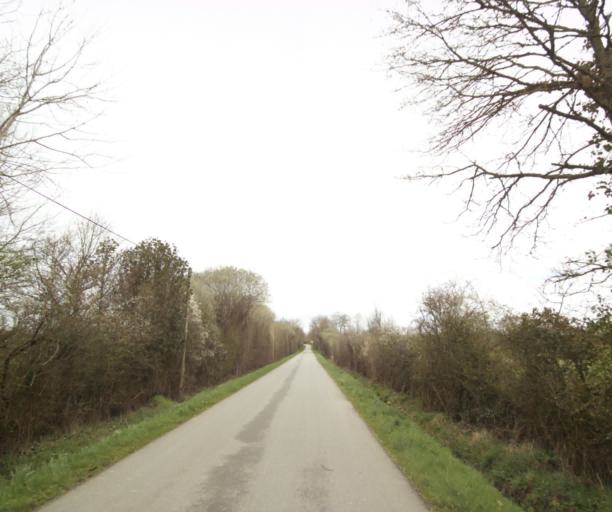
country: FR
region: Pays de la Loire
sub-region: Departement de la Loire-Atlantique
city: Bouvron
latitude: 47.4357
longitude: -1.8895
